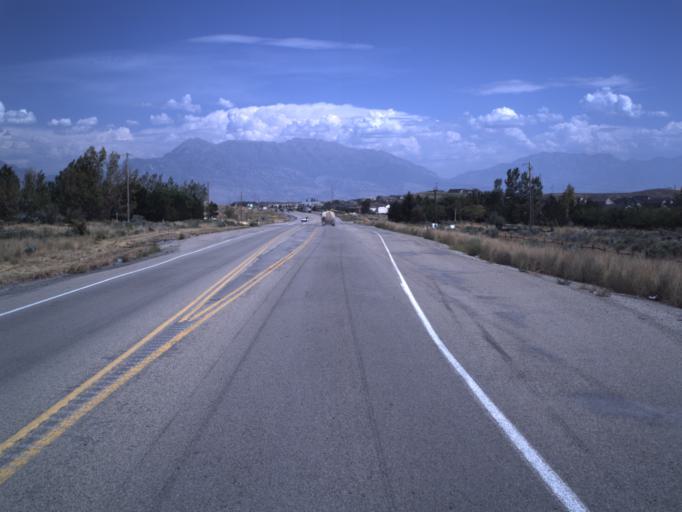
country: US
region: Utah
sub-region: Utah County
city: Eagle Mountain
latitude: 40.3803
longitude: -111.9837
